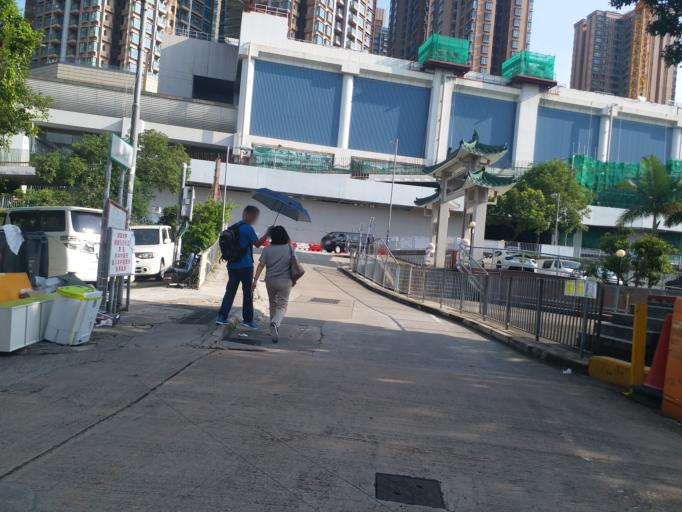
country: HK
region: Yuen Long
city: Yuen Long Kau Hui
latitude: 22.4469
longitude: 114.0372
